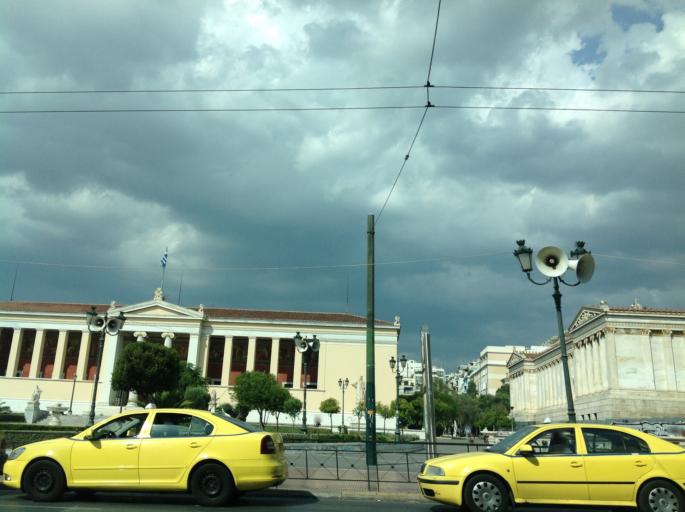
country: GR
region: Attica
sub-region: Nomarchia Athinas
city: Athens
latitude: 37.9801
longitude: 23.7331
